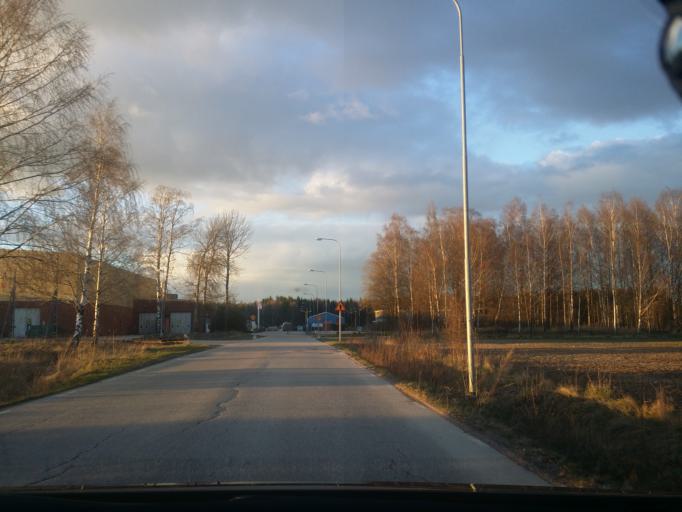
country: SE
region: Vaestmanland
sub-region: Vasteras
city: Hokasen
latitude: 59.6495
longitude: 16.5898
